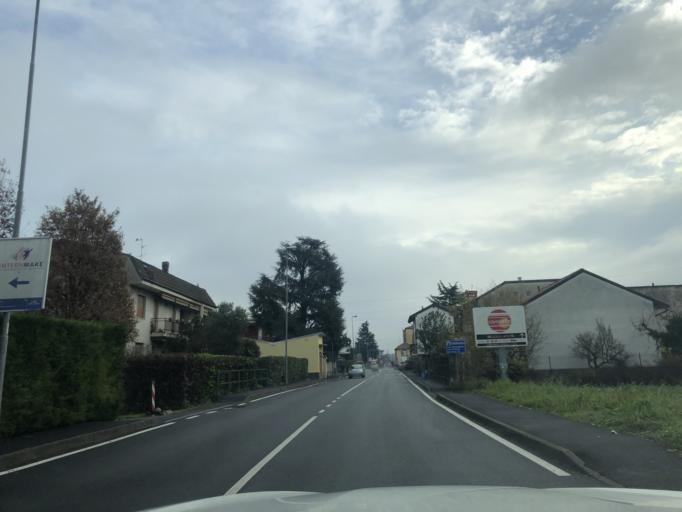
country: IT
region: Lombardy
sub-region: Citta metropolitana di Milano
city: Cologno Monzese
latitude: 45.5482
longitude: 9.2782
